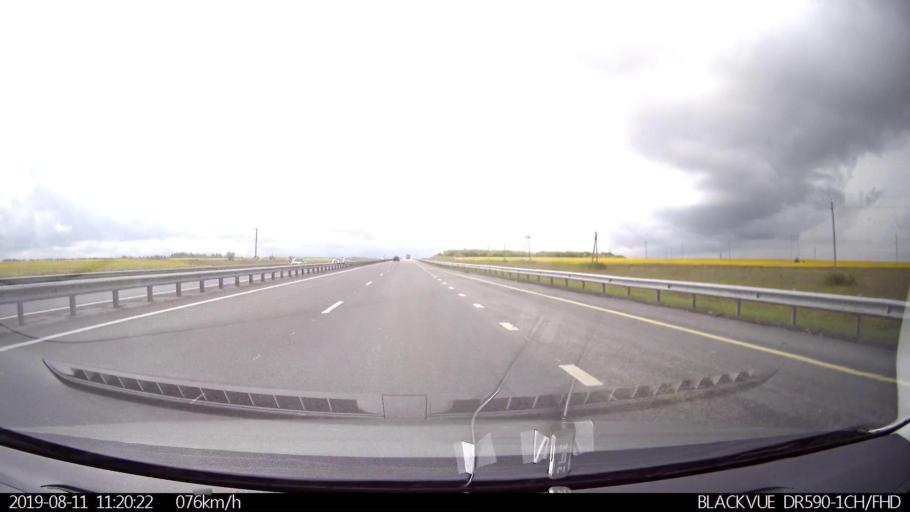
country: RU
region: Ulyanovsk
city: Novoul'yanovsk
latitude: 54.1585
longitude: 48.2645
